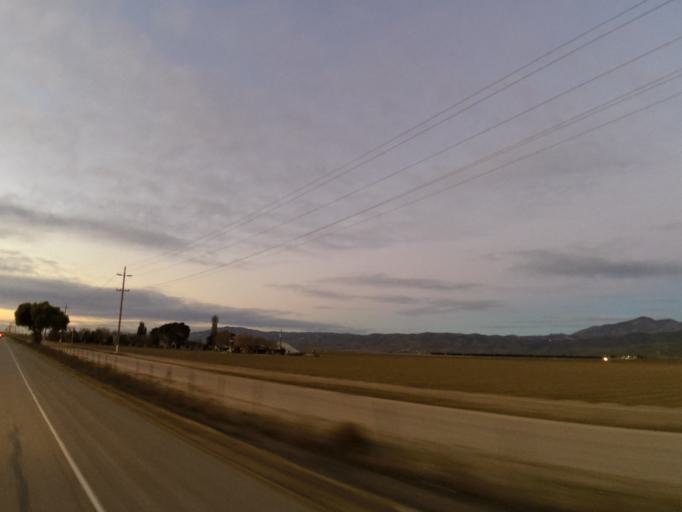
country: US
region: California
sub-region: Monterey County
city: Greenfield
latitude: 36.3538
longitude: -121.2684
